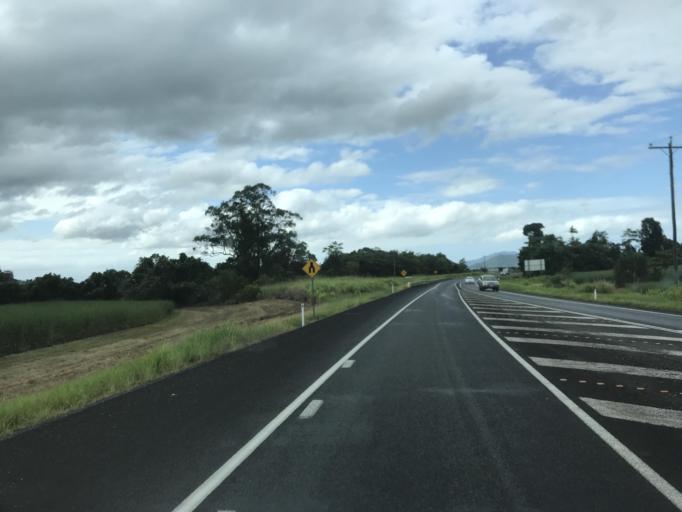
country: AU
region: Queensland
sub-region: Cassowary Coast
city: Innisfail
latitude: -17.7788
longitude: 146.0283
